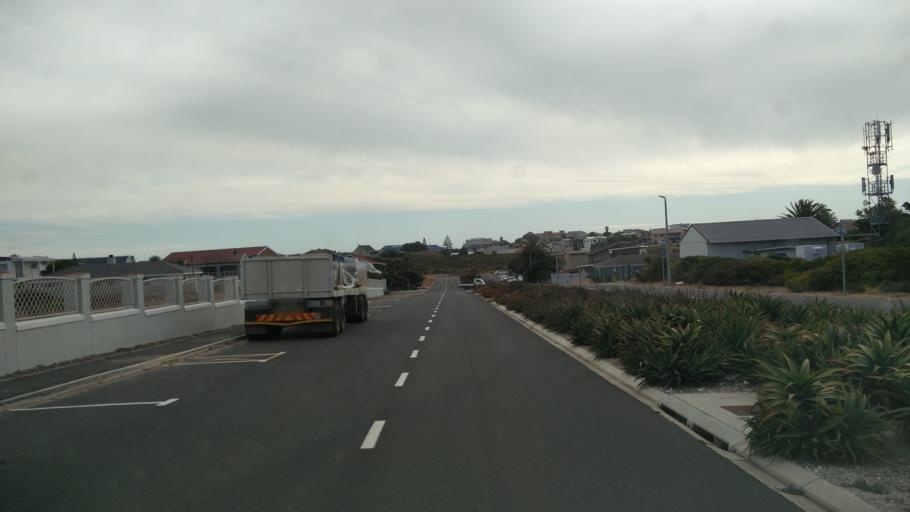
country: ZA
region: Western Cape
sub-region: City of Cape Town
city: Atlantis
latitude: -33.3477
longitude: 18.1569
